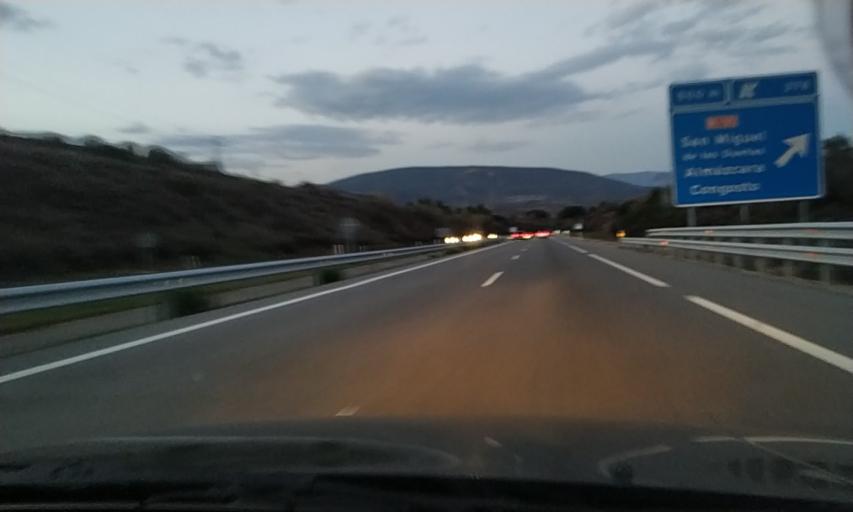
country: ES
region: Castille and Leon
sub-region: Provincia de Leon
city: Congosto
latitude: 42.5854
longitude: -6.5270
